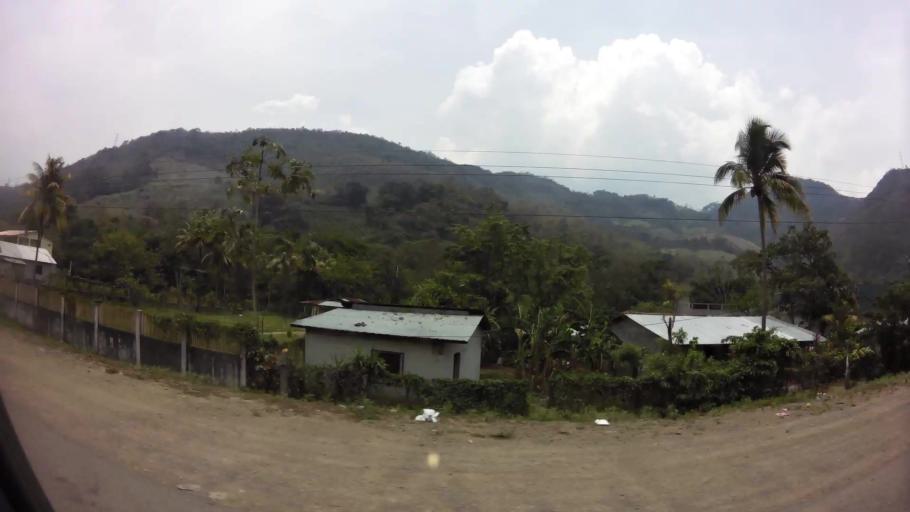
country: HN
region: Comayagua
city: Taulabe
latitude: 14.7340
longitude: -87.9644
